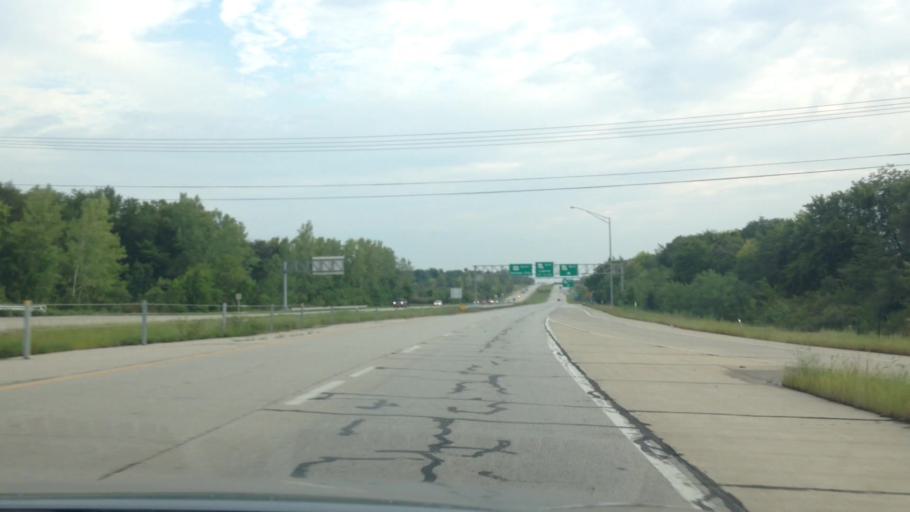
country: US
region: Missouri
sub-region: Clay County
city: Gladstone
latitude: 39.2672
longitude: -94.5851
